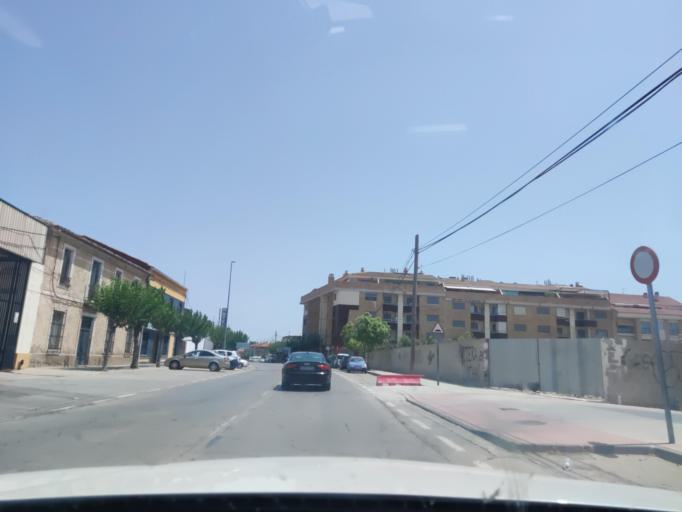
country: ES
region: Castille-La Mancha
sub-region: Provincia de Albacete
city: Hellin
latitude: 38.5072
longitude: -1.6885
